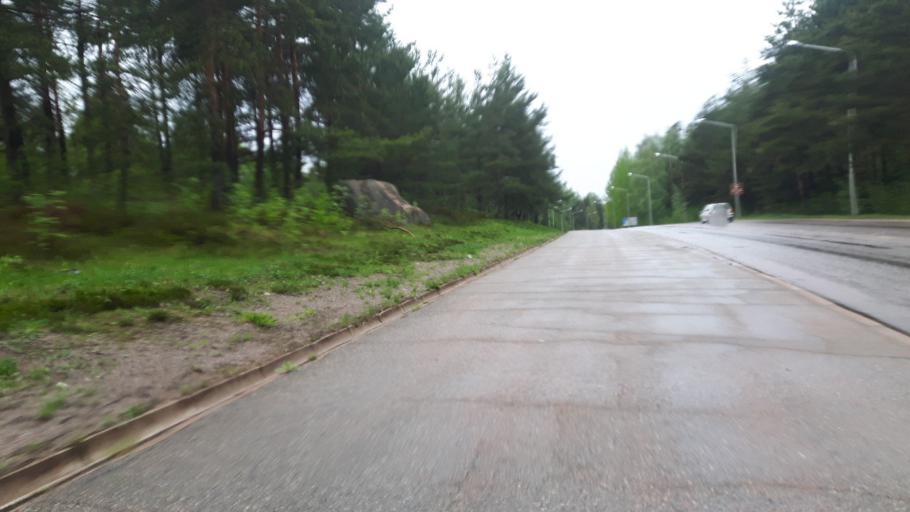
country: FI
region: Kymenlaakso
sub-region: Kotka-Hamina
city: Kotka
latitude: 60.4910
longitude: 26.9020
